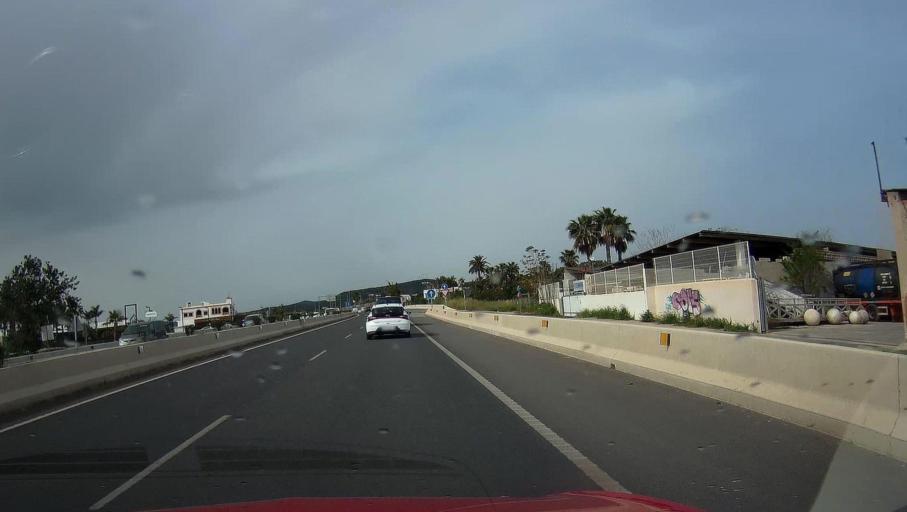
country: ES
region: Balearic Islands
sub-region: Illes Balears
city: Ibiza
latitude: 38.9322
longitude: 1.4438
